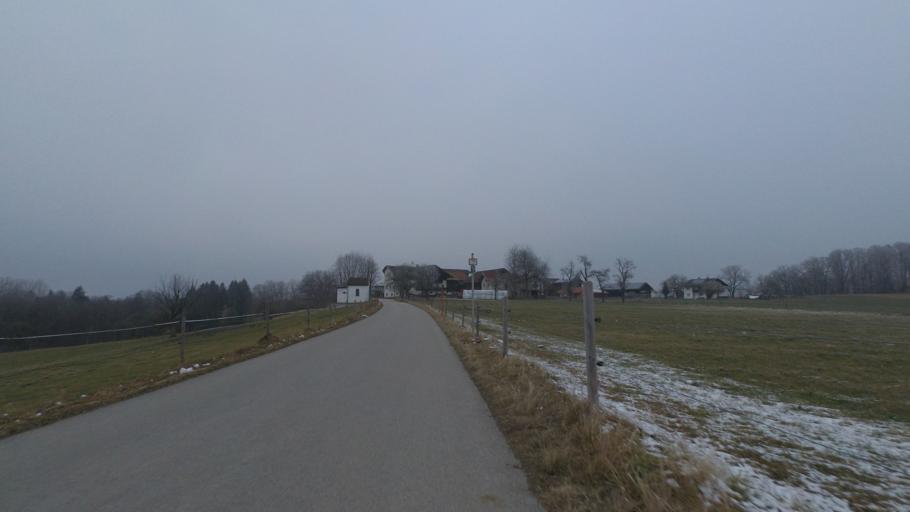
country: DE
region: Bavaria
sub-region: Upper Bavaria
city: Chieming
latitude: 47.8890
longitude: 12.5558
